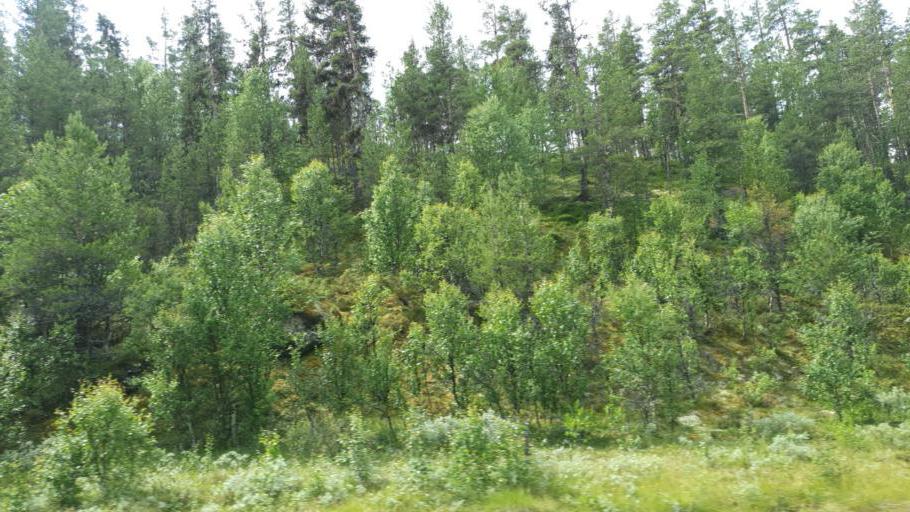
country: NO
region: Oppland
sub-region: Vaga
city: Vagamo
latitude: 61.7126
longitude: 9.0526
